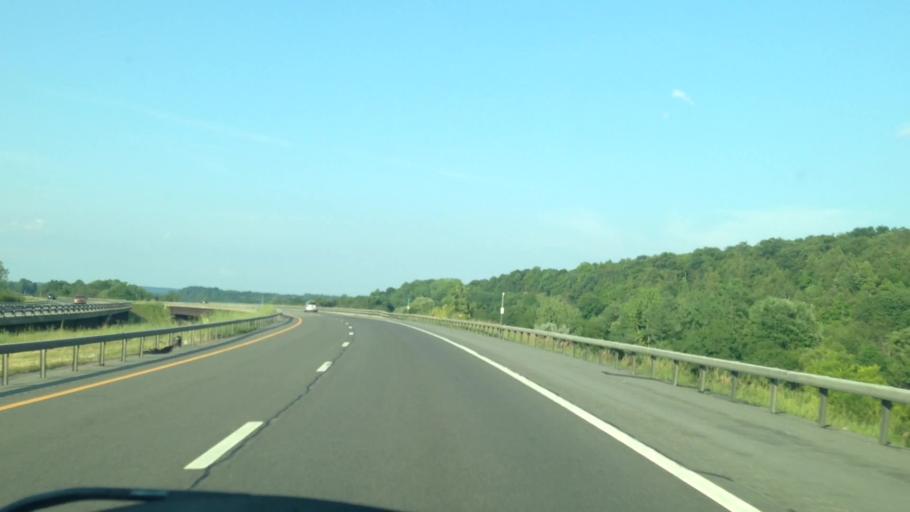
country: US
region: New York
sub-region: Onondaga County
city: Nedrow
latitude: 43.0032
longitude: -76.0954
